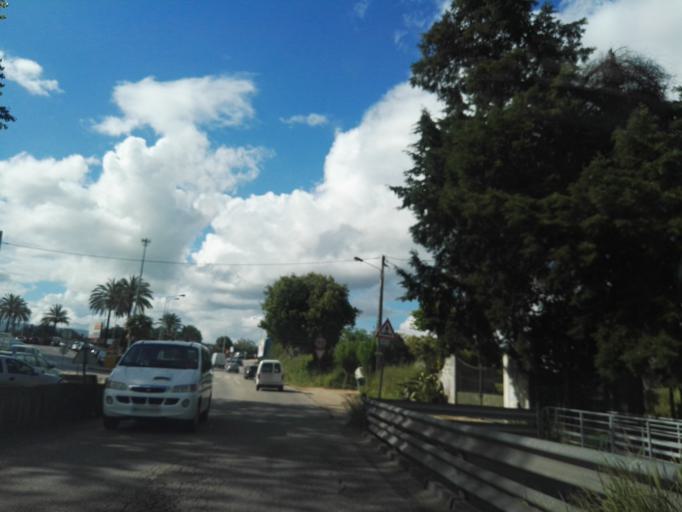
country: PT
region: Santarem
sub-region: Torres Novas
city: Riachos
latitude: 39.4648
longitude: -8.5231
